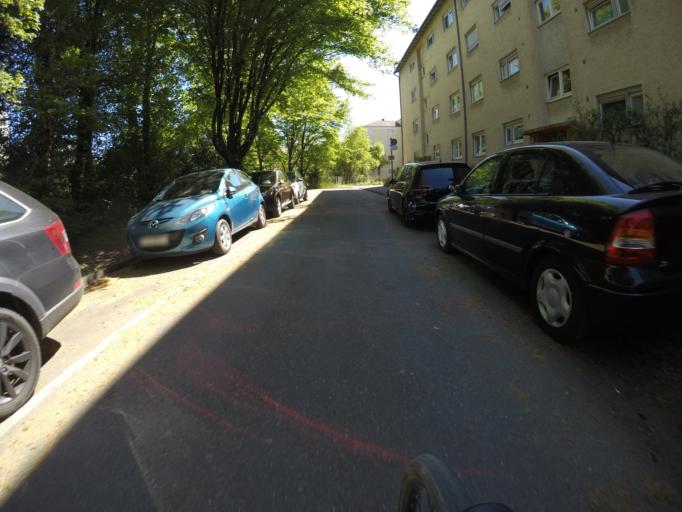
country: DE
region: Baden-Wuerttemberg
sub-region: Regierungsbezirk Stuttgart
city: Stuttgart-Ost
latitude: 48.8084
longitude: 9.2323
